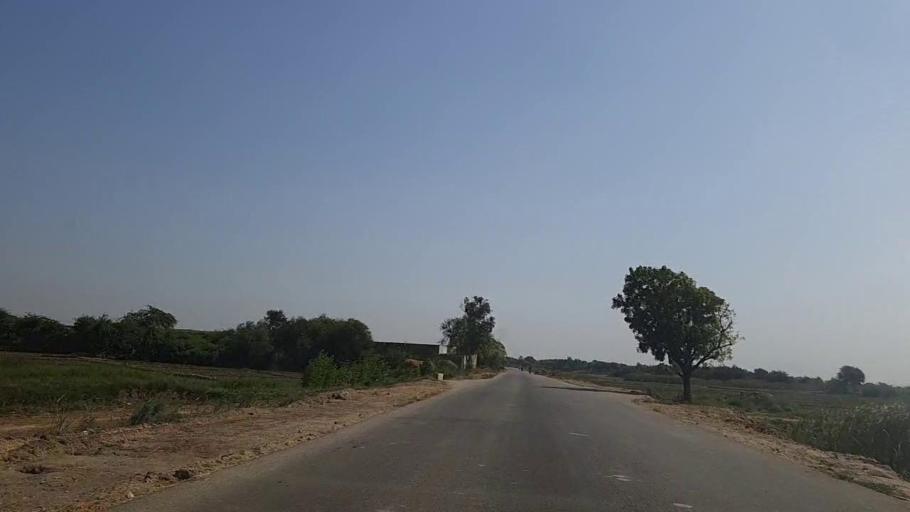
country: PK
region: Sindh
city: Daro Mehar
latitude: 24.7688
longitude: 68.2123
